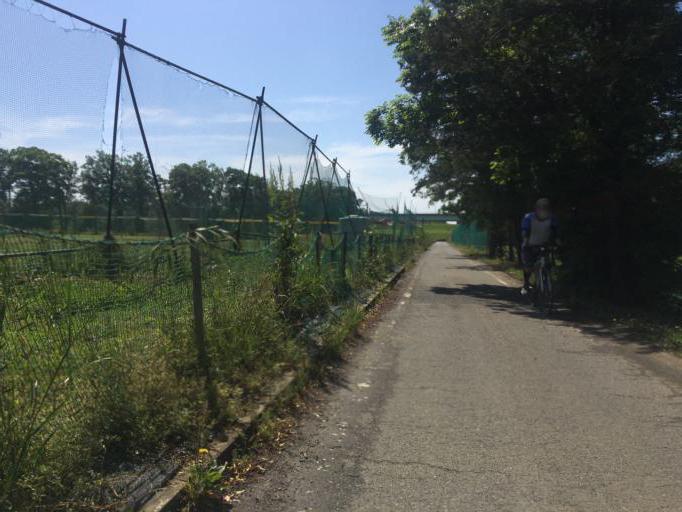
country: JP
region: Saitama
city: Shiki
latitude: 35.8589
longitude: 139.5902
